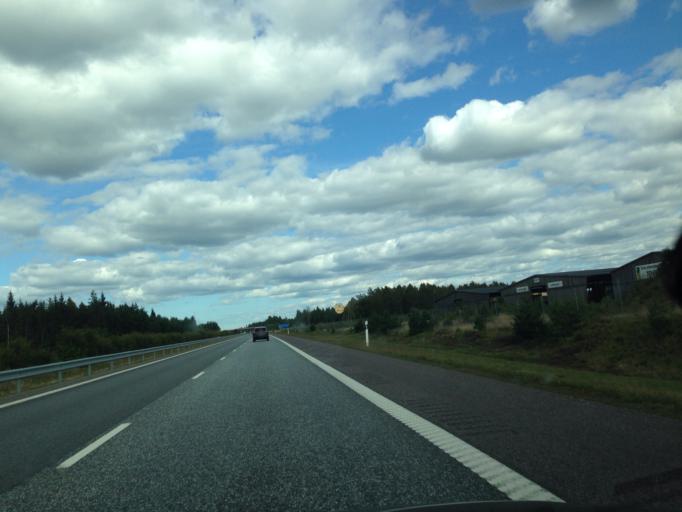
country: SE
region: Joenkoeping
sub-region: Vaggeryds Kommun
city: Vaggeryd
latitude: 57.4854
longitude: 14.1033
